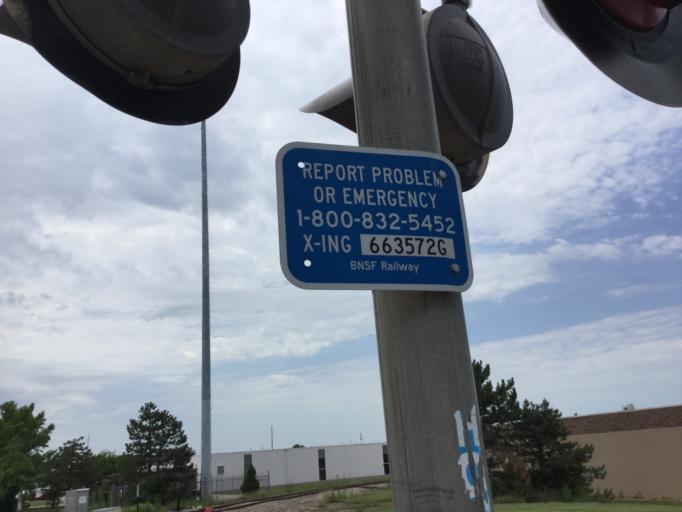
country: US
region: Kansas
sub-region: Johnson County
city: Lenexa
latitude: 38.9390
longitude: -94.7518
